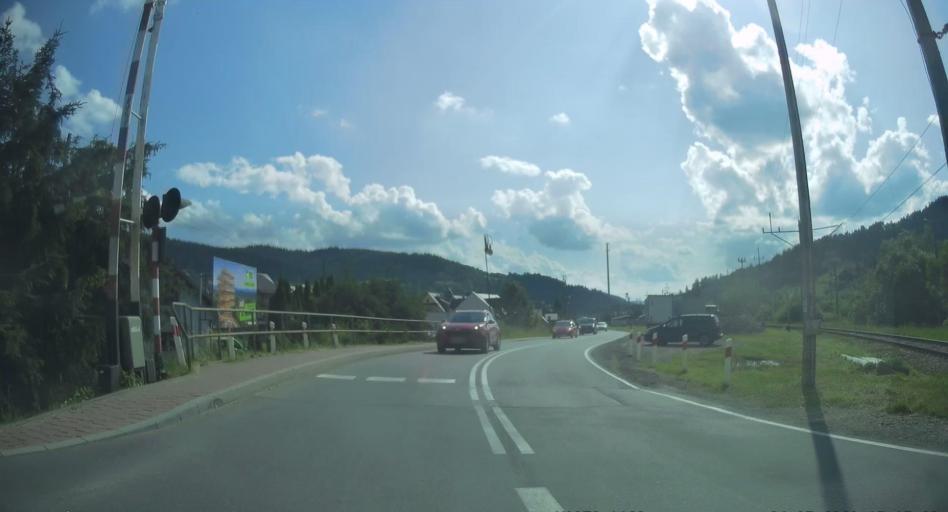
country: PL
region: Lesser Poland Voivodeship
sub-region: Powiat nowosadecki
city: Muszyna
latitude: 49.3704
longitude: 20.9454
